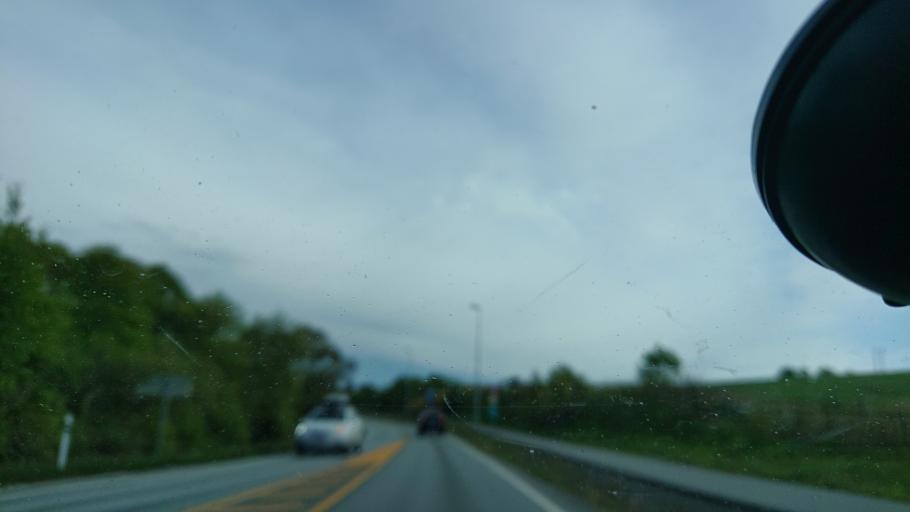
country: NO
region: Rogaland
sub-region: Sola
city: Tananger
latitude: 58.9440
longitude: 5.5989
